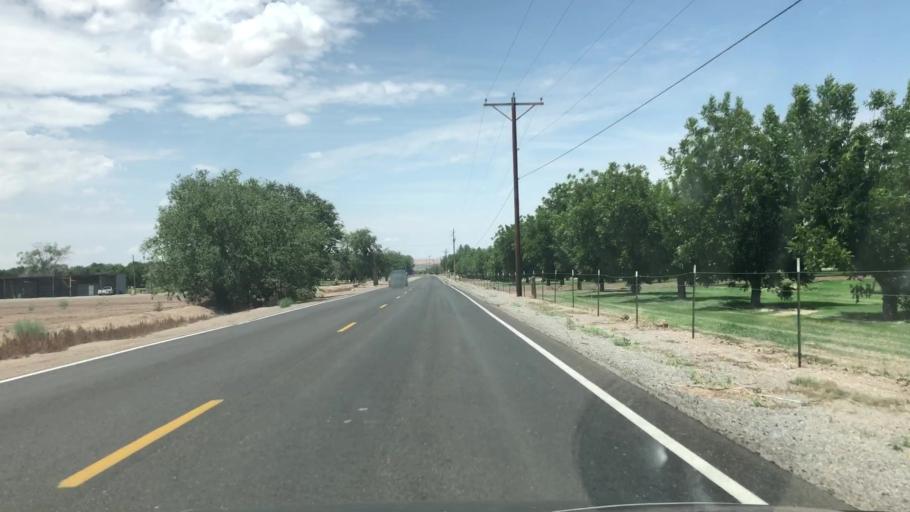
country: US
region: Texas
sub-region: El Paso County
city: Canutillo
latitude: 31.9203
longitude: -106.6361
